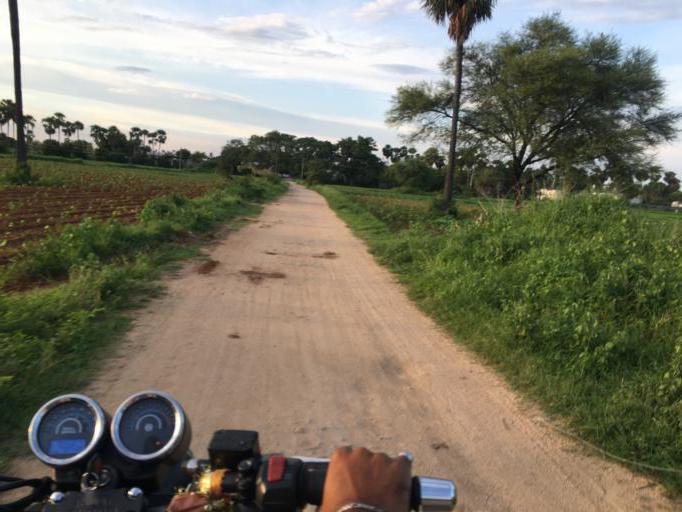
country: IN
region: Telangana
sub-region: Nalgonda
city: Nalgonda
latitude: 17.1713
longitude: 79.4173
